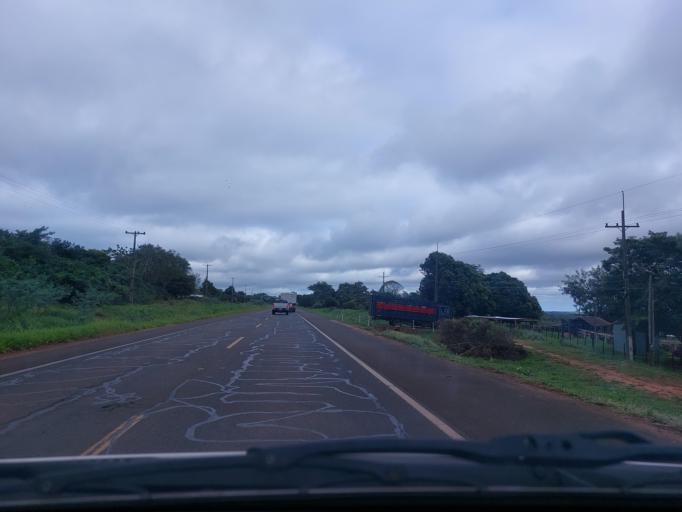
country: PY
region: San Pedro
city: Guayaybi
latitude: -24.6497
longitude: -56.3845
